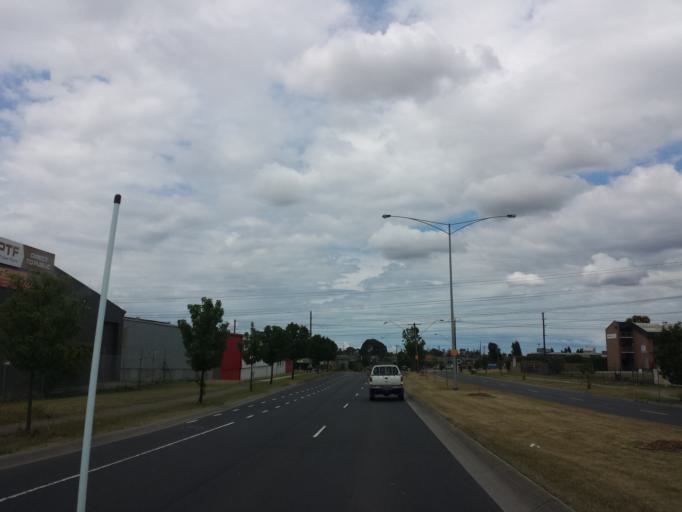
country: AU
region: Victoria
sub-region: Whittlesea
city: Thomastown
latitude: -37.6904
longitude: 145.0023
